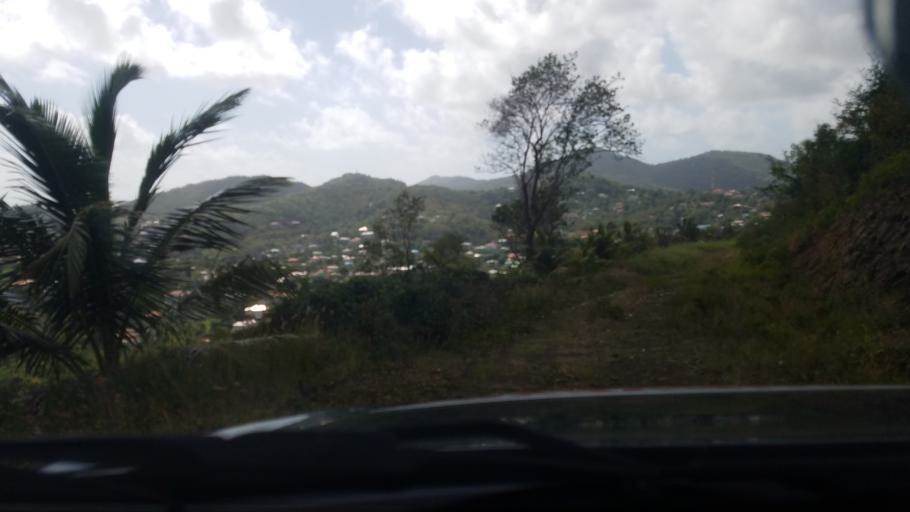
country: LC
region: Gros-Islet
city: Gros Islet
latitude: 14.0653
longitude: -60.9485
